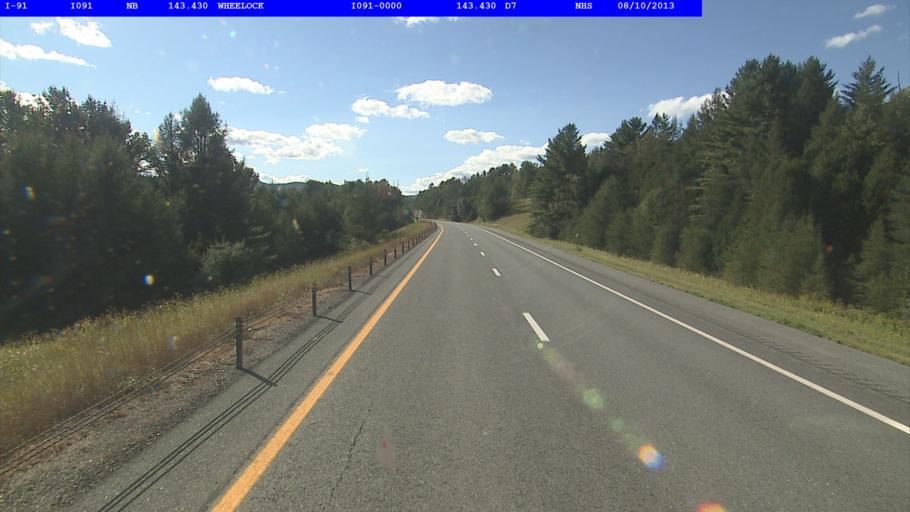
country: US
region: Vermont
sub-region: Caledonia County
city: Lyndonville
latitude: 44.5870
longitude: -72.0745
